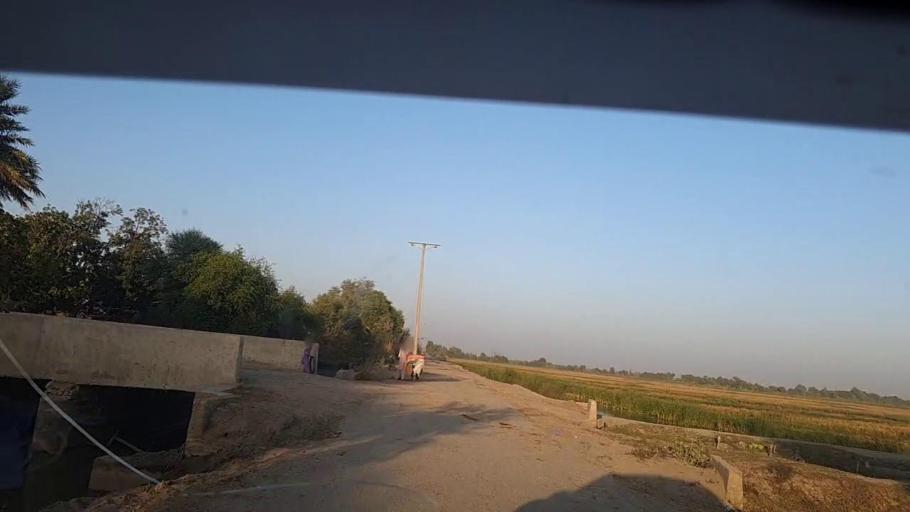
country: PK
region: Sindh
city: Ratodero
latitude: 27.8884
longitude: 68.2166
